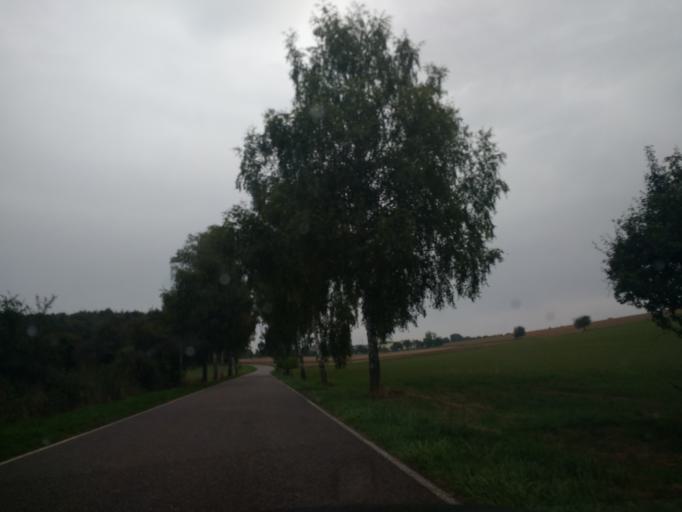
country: DE
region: Saarland
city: Perl
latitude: 49.4975
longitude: 6.3985
